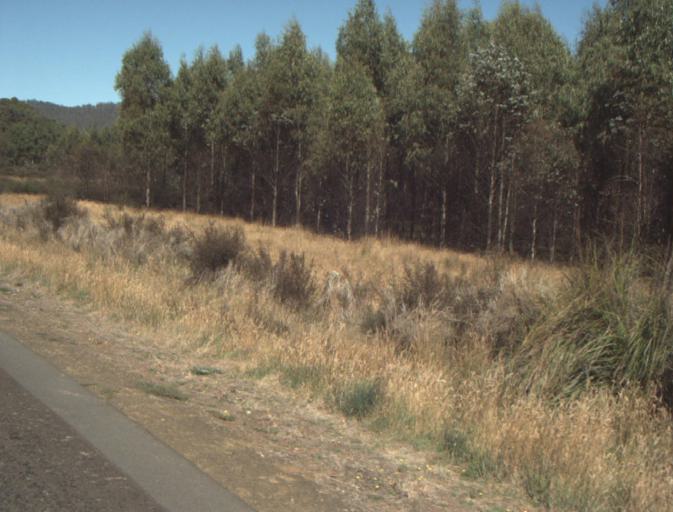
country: AU
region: Tasmania
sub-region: Launceston
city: Newstead
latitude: -41.3244
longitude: 147.3191
